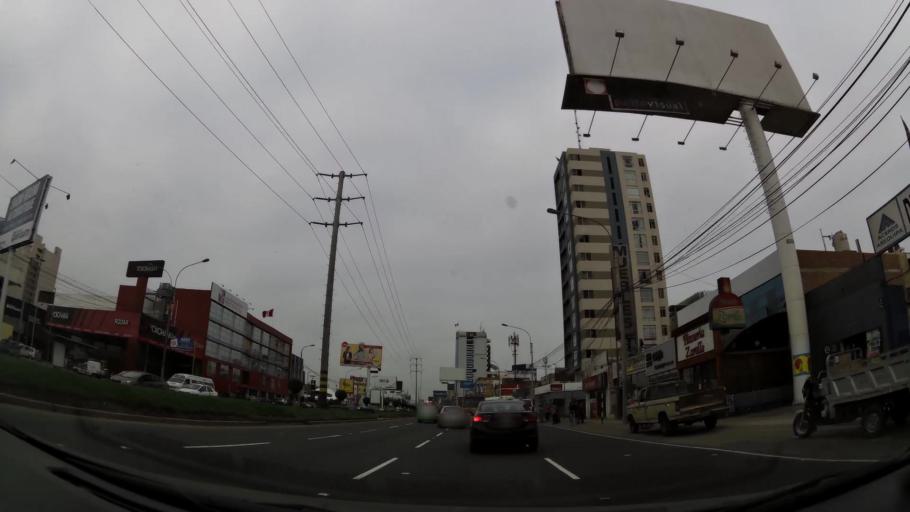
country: PE
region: Callao
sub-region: Callao
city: Callao
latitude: -12.0780
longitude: -77.0916
